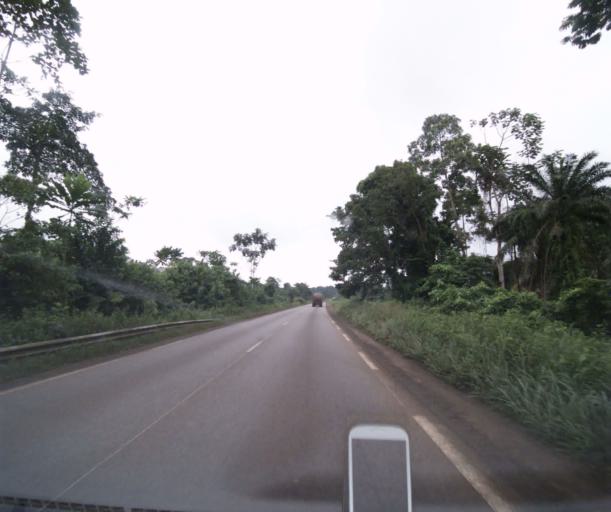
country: CM
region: Littoral
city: Edea
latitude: 3.8128
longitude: 10.3097
